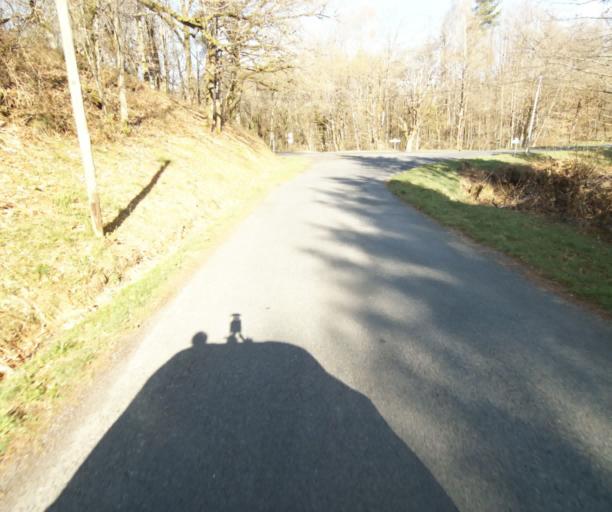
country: FR
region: Limousin
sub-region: Departement de la Correze
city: Correze
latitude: 45.2771
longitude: 1.8806
